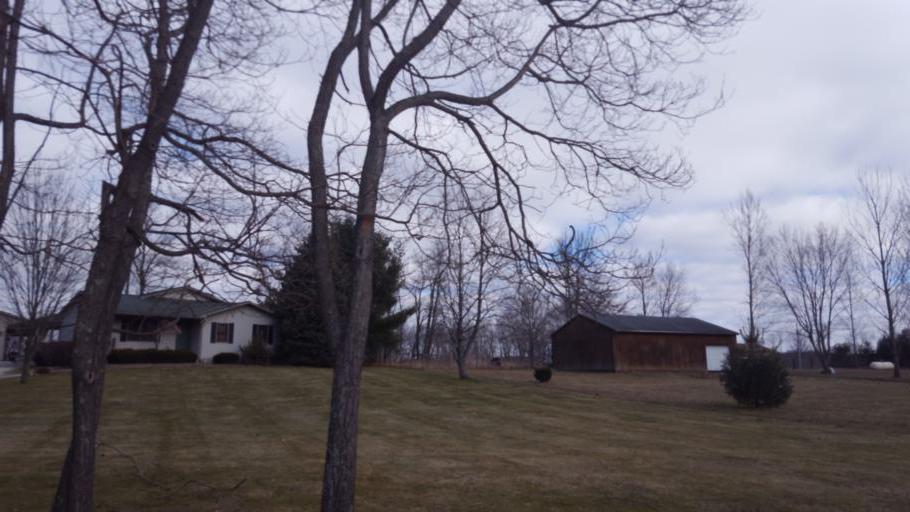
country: US
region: Ohio
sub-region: Knox County
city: Fredericktown
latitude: 40.5336
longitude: -82.5320
